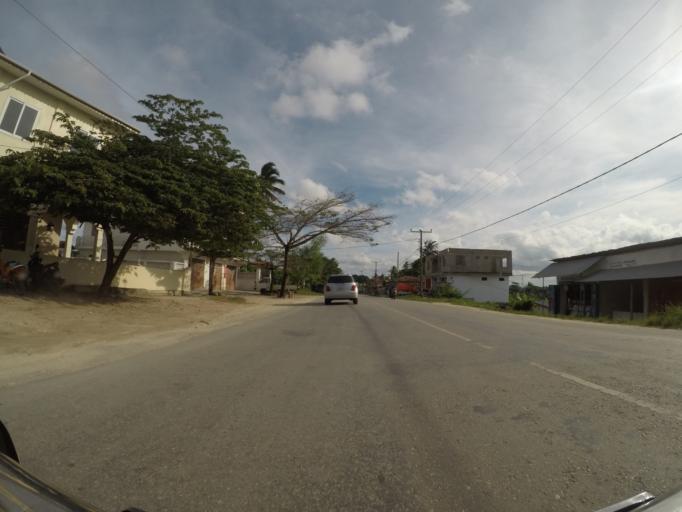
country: TZ
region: Pemba South
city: Chake Chake
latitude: -5.2292
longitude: 39.7756
